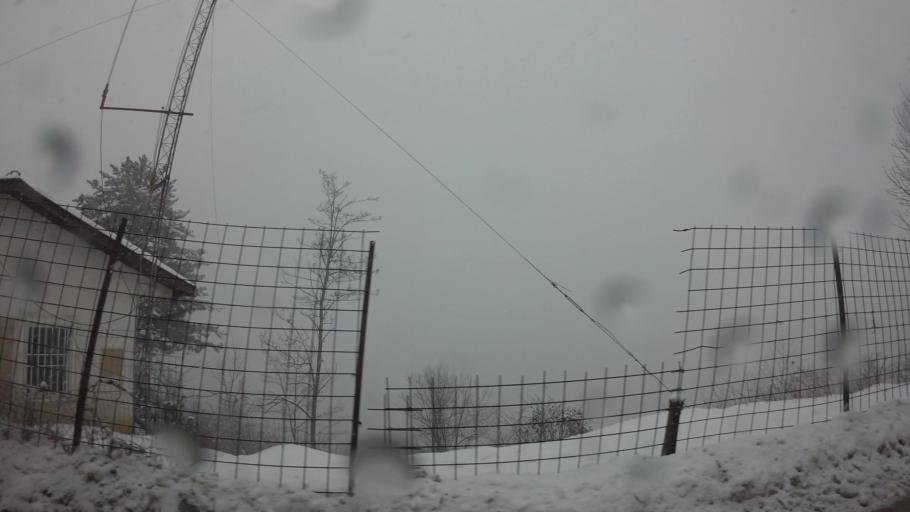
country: BA
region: Federation of Bosnia and Herzegovina
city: Kobilja Glava
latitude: 43.8544
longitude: 18.4451
